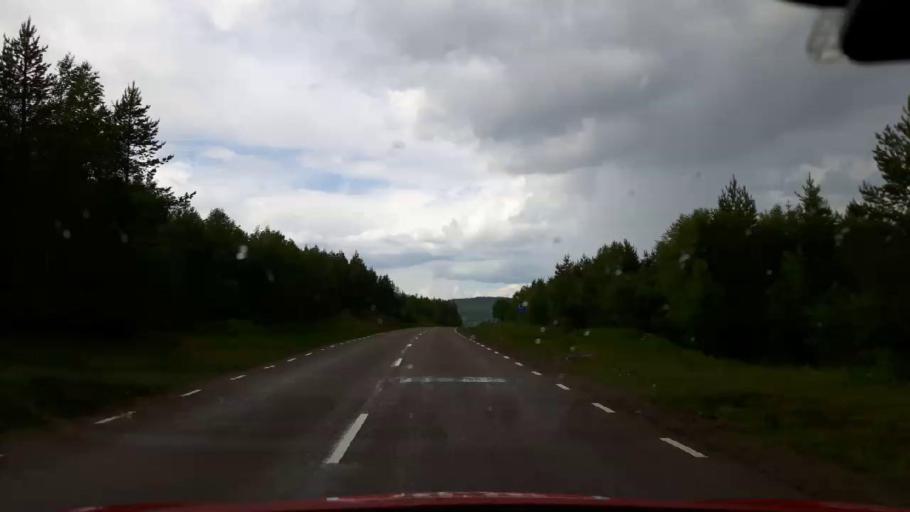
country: SE
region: Jaemtland
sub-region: Krokoms Kommun
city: Valla
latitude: 63.8915
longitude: 14.2672
